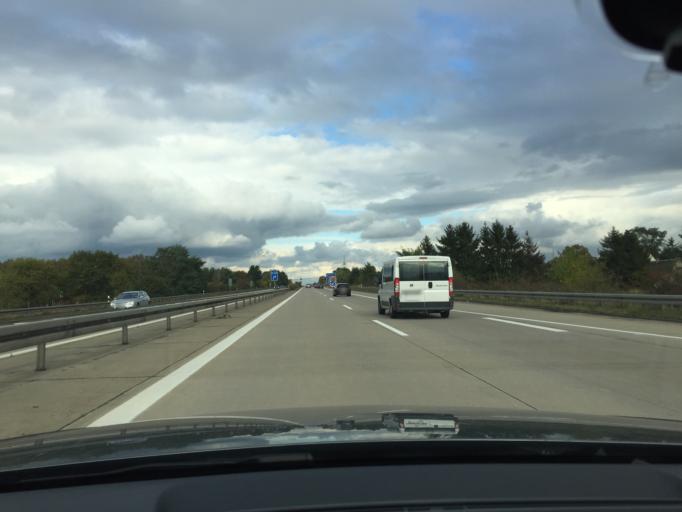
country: DE
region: Brandenburg
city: Ruhland
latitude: 51.4607
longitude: 13.8546
